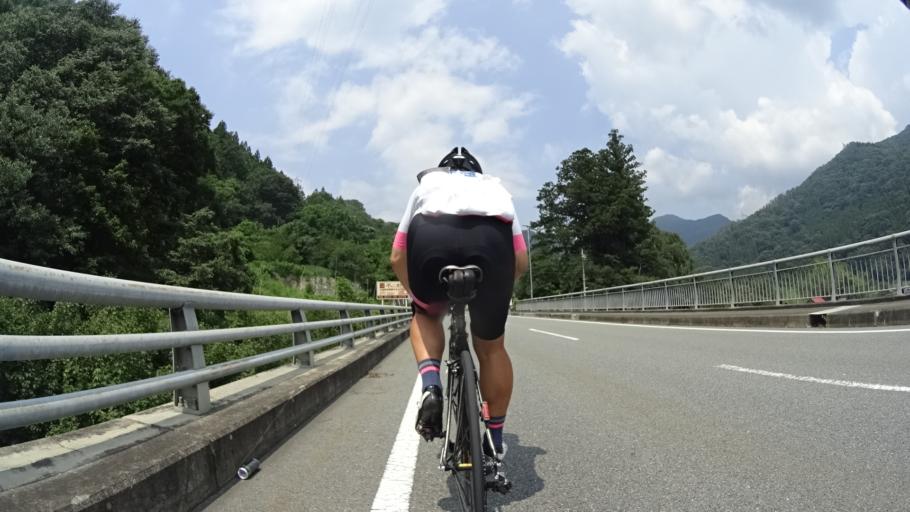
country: JP
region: Gunma
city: Tomioka
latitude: 36.0804
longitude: 138.7760
